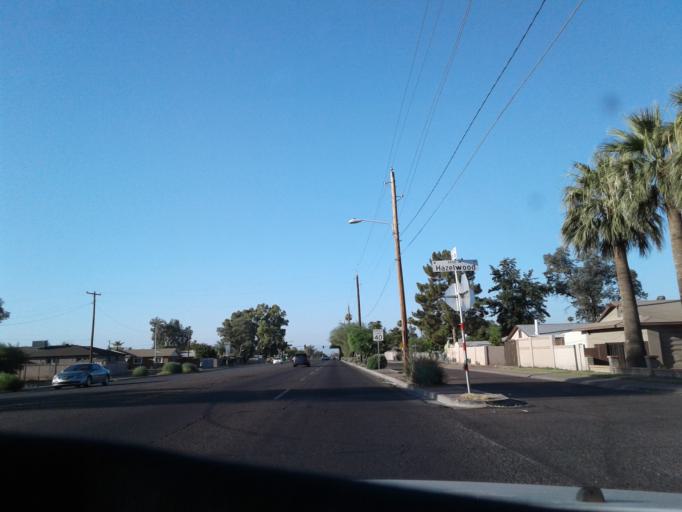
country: US
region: Arizona
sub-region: Maricopa County
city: Glendale
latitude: 33.5047
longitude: -112.1865
